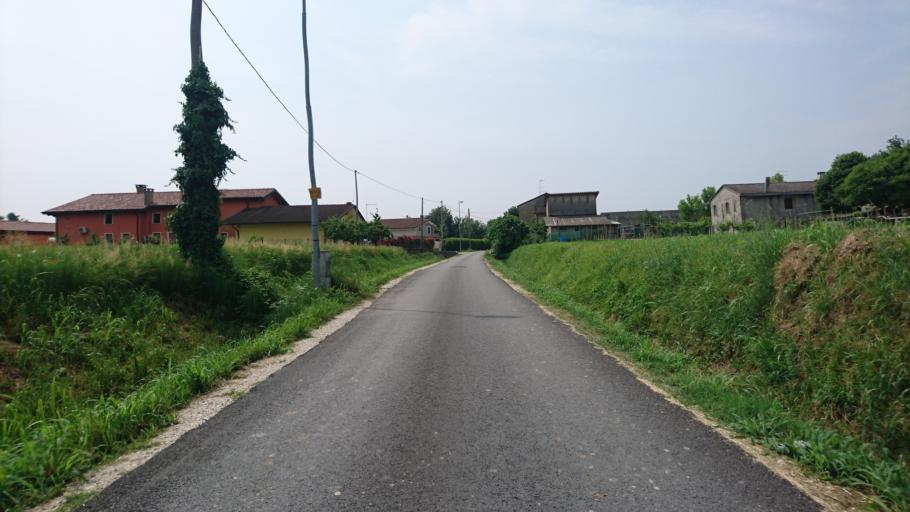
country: IT
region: Veneto
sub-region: Provincia di Padova
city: Polverara
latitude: 45.3102
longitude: 11.9482
